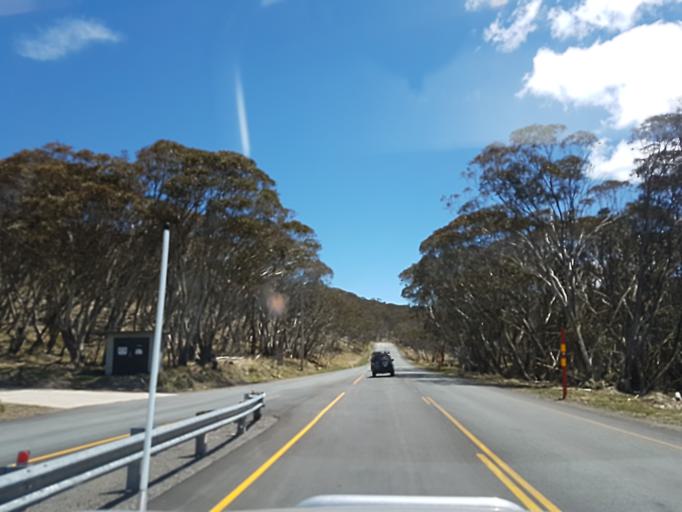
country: AU
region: Victoria
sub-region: Alpine
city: Mount Beauty
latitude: -37.0216
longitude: 147.1963
